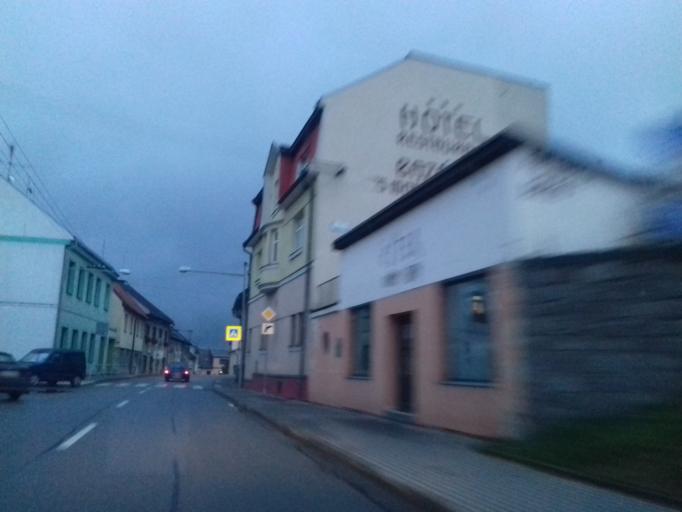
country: CZ
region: Pardubicky
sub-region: Okres Svitavy
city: Bystre
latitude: 49.6298
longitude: 16.3450
